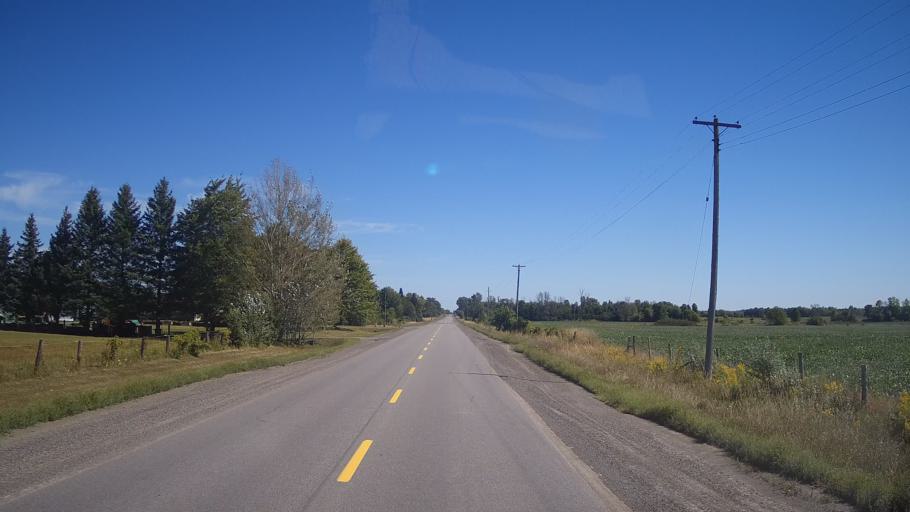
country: CA
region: Ontario
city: Bells Corners
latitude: 45.0319
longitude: -75.7192
